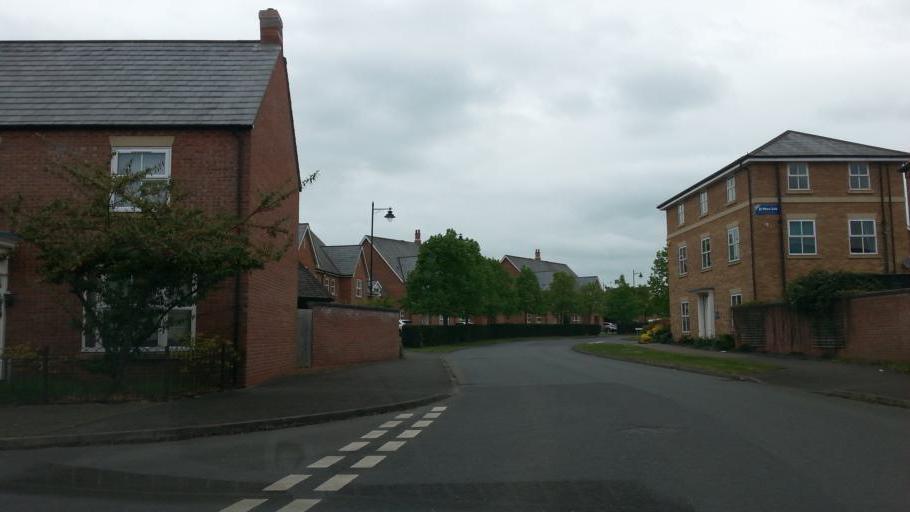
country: GB
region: England
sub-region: Lincolnshire
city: Bourne
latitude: 52.7562
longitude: -0.3706
